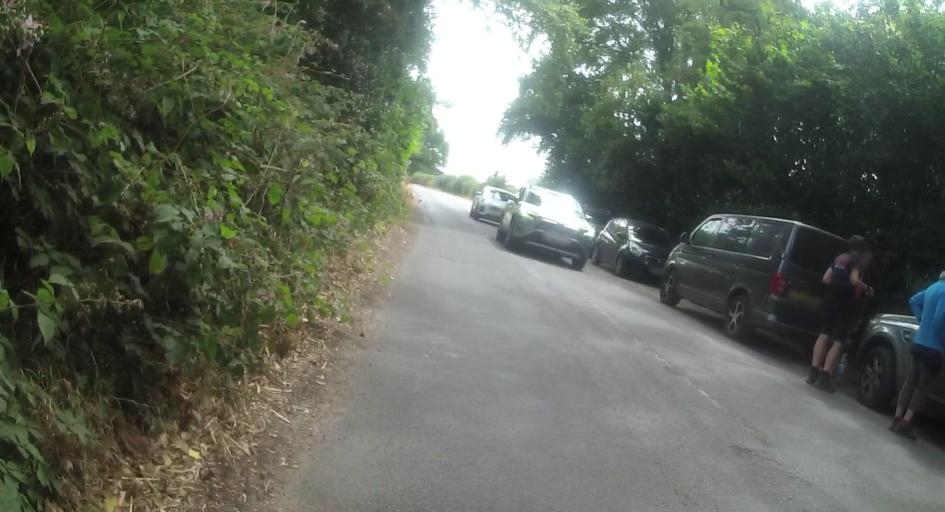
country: GB
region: England
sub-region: Dorset
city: Bovington Camp
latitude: 50.7027
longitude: -2.2784
